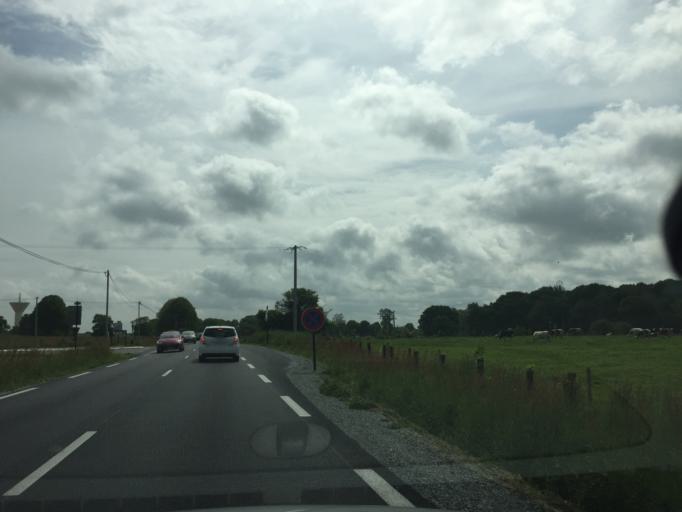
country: FR
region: Brittany
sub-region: Departement des Cotes-d'Armor
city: Crehen
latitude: 48.5658
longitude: -2.1957
